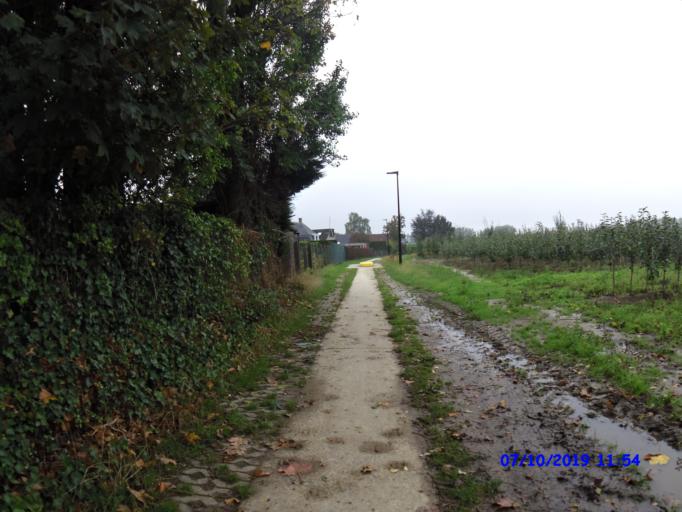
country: BE
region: Flanders
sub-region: Provincie Oost-Vlaanderen
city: Oosterzele
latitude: 50.9429
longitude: 3.7815
